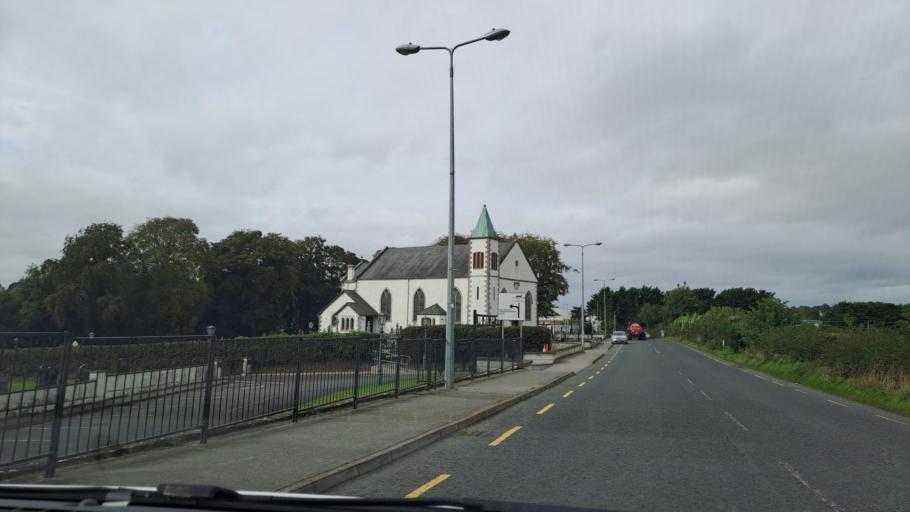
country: IE
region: Ulster
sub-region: An Cabhan
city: Bailieborough
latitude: 53.9960
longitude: -6.9000
